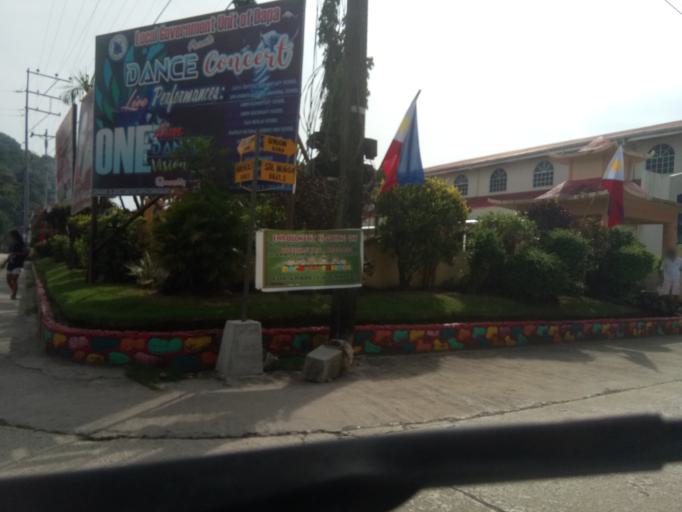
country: PH
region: Caraga
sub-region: Province of Surigao del Norte
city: Dapa
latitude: 9.7573
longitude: 126.0526
